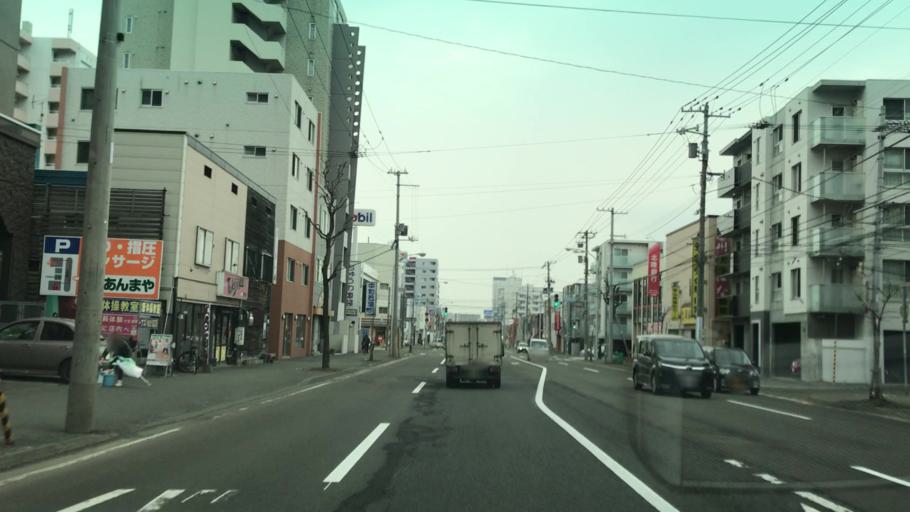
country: JP
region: Hokkaido
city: Sapporo
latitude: 43.0723
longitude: 141.3007
